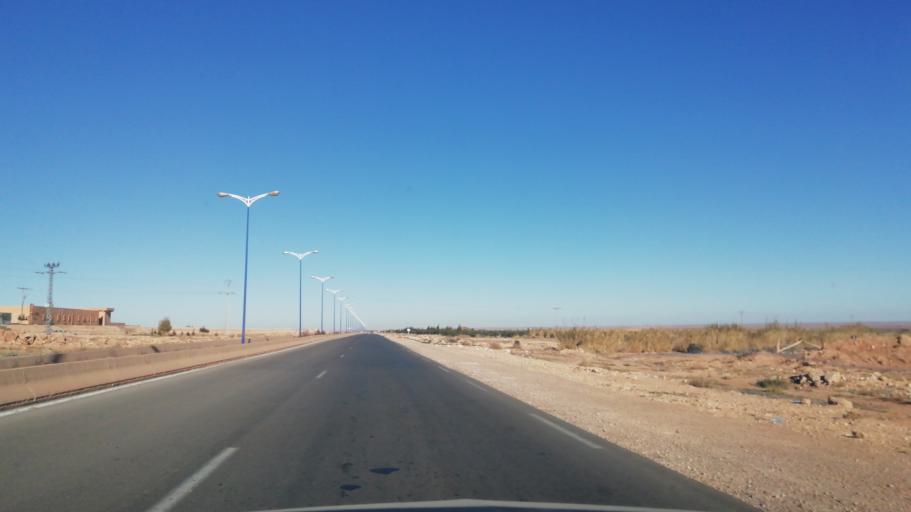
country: DZ
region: Wilaya de Naama
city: Naama
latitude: 33.5458
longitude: -0.2484
